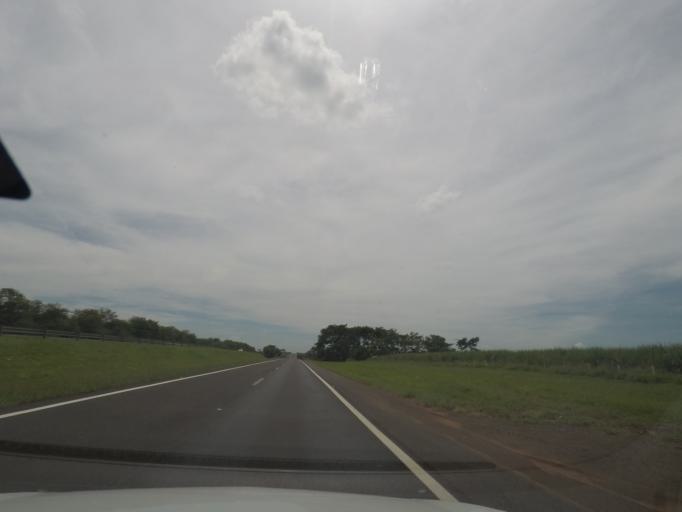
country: BR
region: Sao Paulo
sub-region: Bebedouro
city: Bebedouro
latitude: -20.9829
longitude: -48.4361
